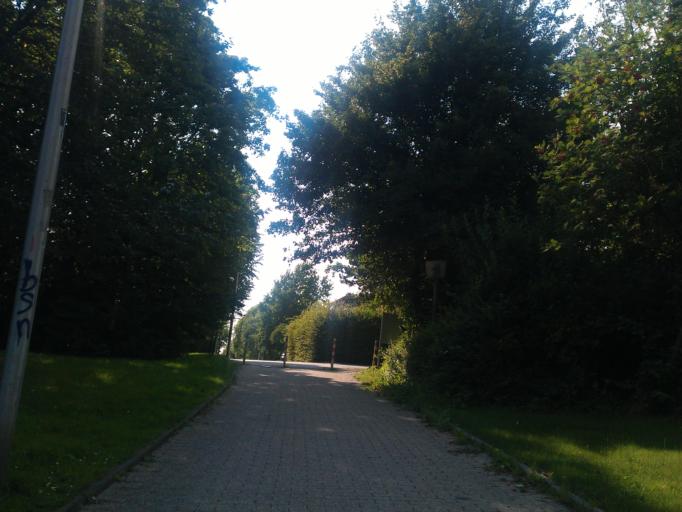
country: NL
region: Limburg
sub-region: Gemeente Vaals
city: Vaals
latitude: 50.7718
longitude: 6.0422
